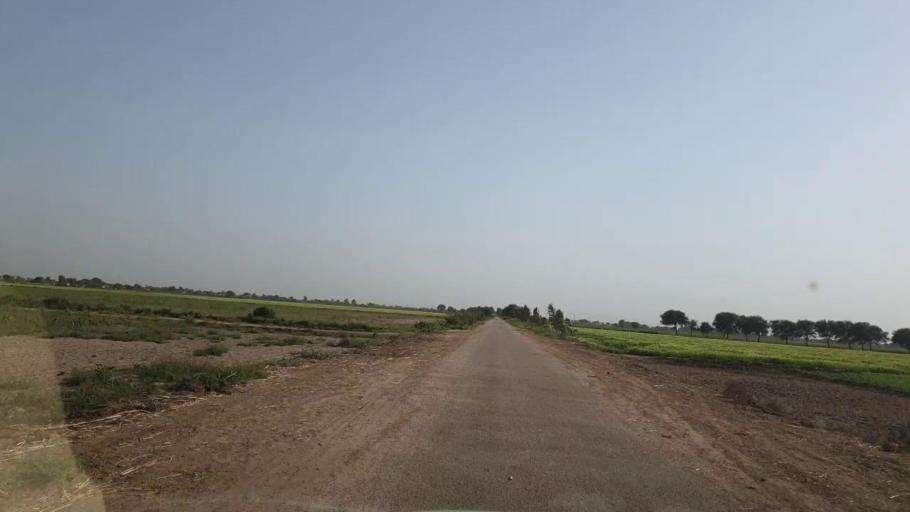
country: PK
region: Sindh
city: Tando Ghulam Ali
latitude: 25.0926
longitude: 68.8530
